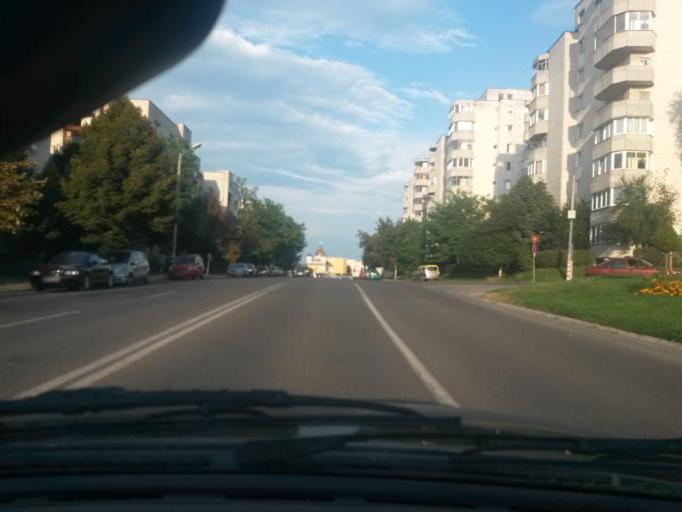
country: RO
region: Mures
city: Targu-Mures
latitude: 46.5336
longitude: 24.5673
